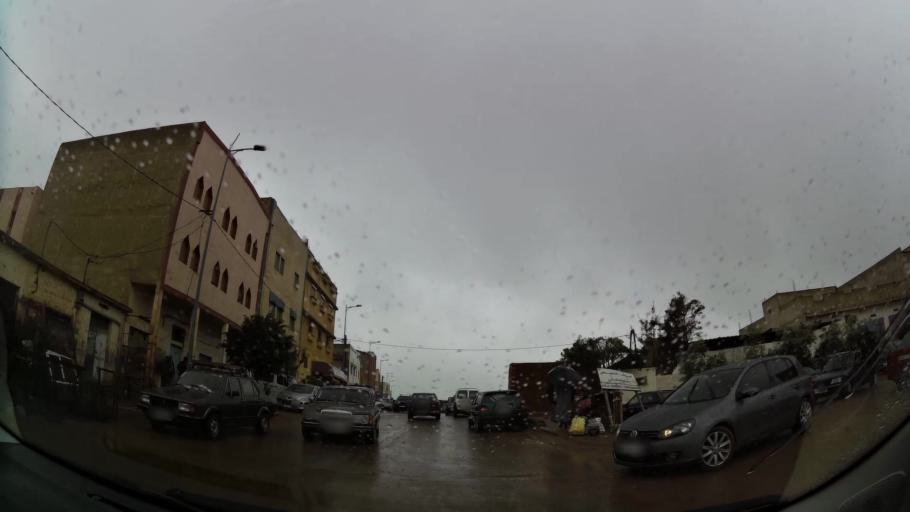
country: MA
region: Oriental
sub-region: Nador
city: Boudinar
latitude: 35.1246
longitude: -3.6289
